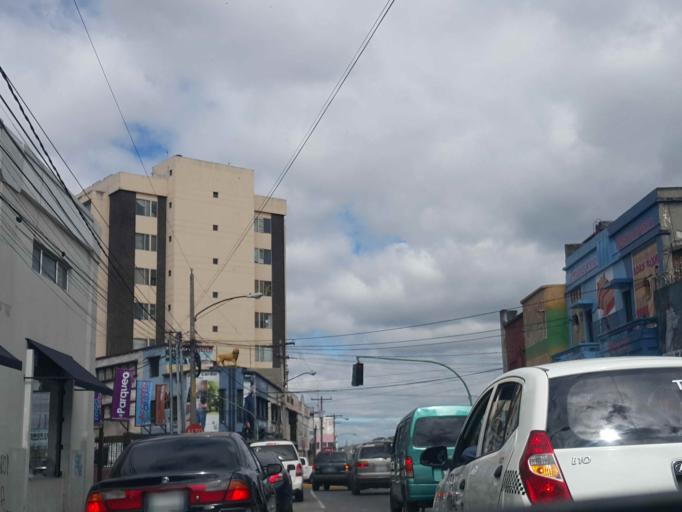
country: GT
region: Guatemala
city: Guatemala City
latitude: 14.6285
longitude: -90.5192
